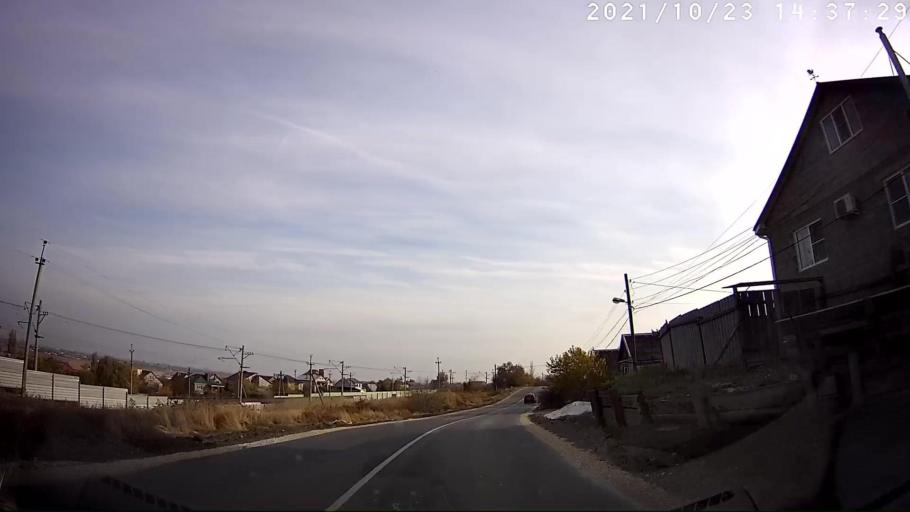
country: RU
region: Volgograd
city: Krasnoslobodsk
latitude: 48.4977
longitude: 44.5489
